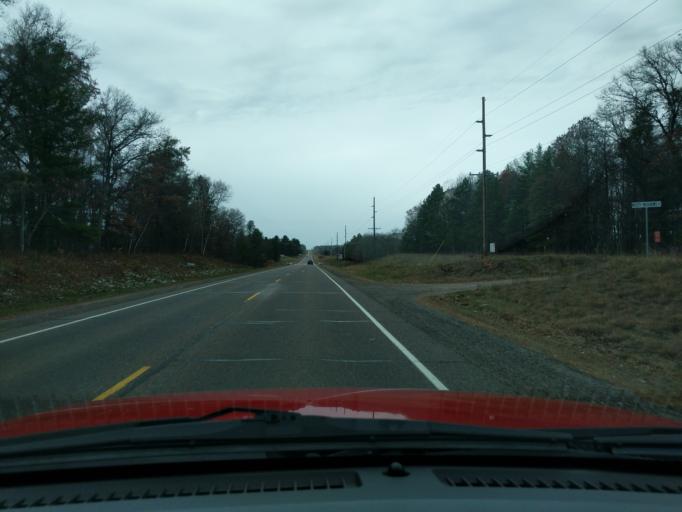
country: US
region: Wisconsin
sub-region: Washburn County
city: Shell Lake
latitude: 45.8151
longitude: -92.0012
